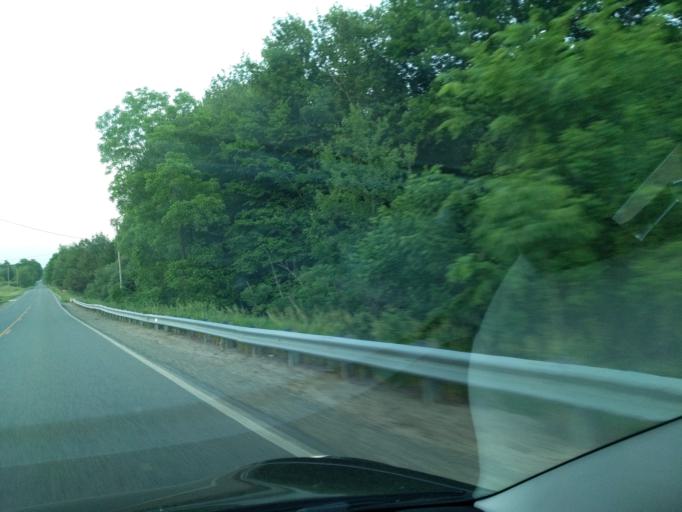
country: US
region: Michigan
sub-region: Barry County
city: Nashville
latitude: 42.5380
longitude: -85.1125
